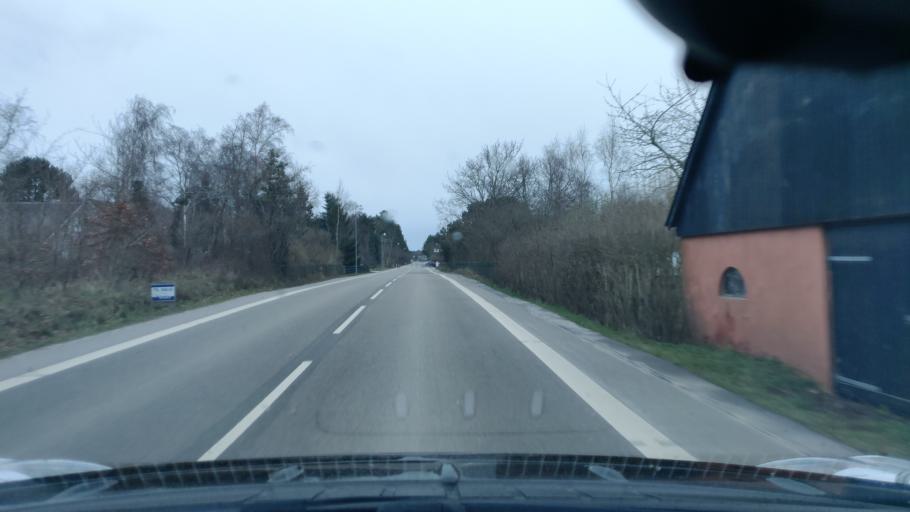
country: DK
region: Zealand
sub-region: Odsherred Kommune
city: Asnaes
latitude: 55.8639
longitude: 11.5327
